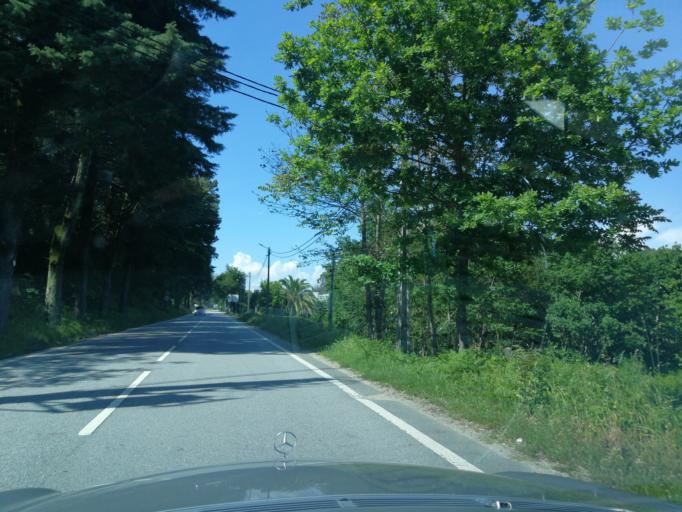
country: PT
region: Braga
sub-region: Braga
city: Adaufe
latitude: 41.5773
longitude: -8.3713
